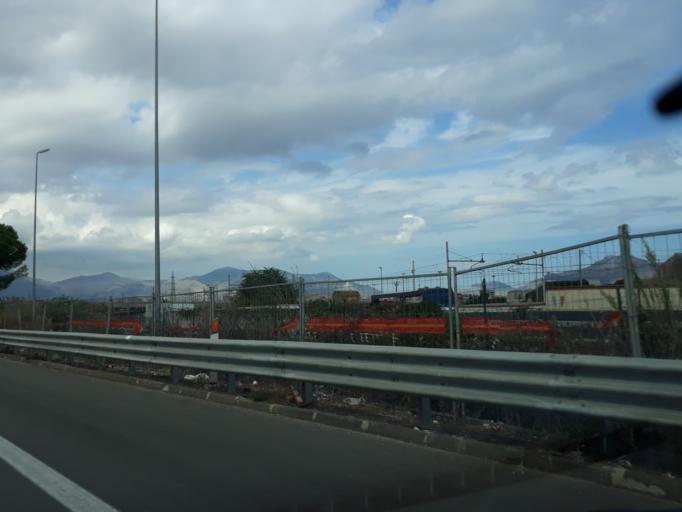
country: IT
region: Sicily
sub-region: Palermo
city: Ciaculli
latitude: 38.0860
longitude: 13.4118
